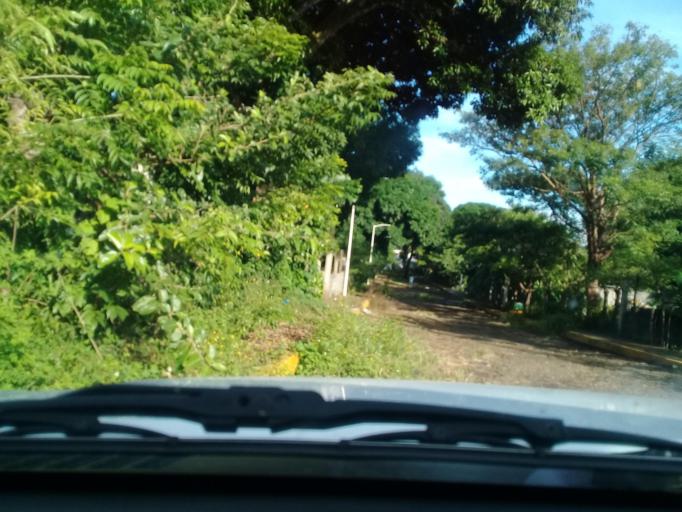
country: MX
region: Veracruz
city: Catemaco
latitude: 18.4301
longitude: -95.1107
